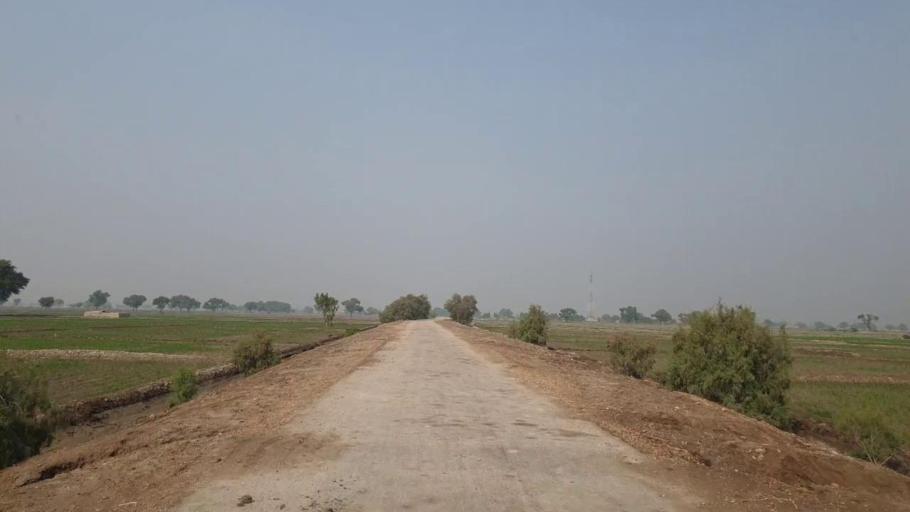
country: PK
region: Sindh
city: Bhan
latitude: 26.4927
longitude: 67.6998
